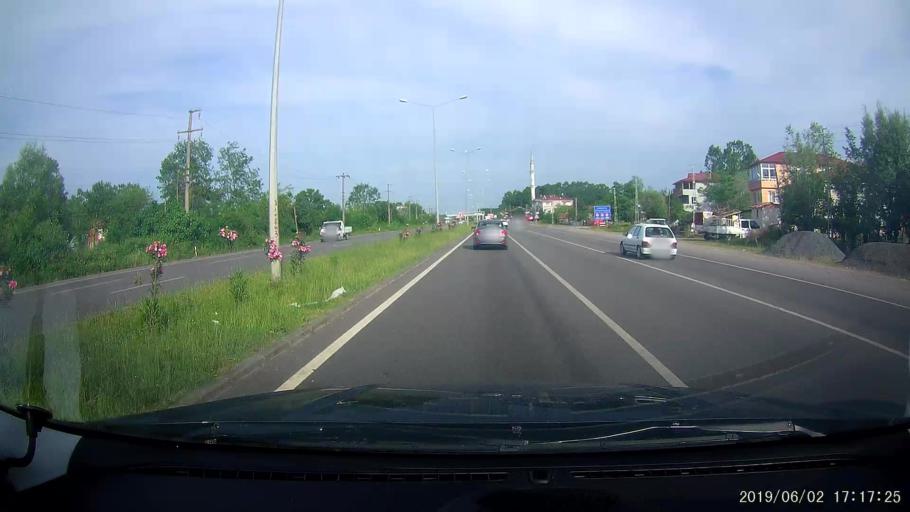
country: TR
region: Samsun
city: Dikbiyik
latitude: 41.2291
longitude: 36.5813
